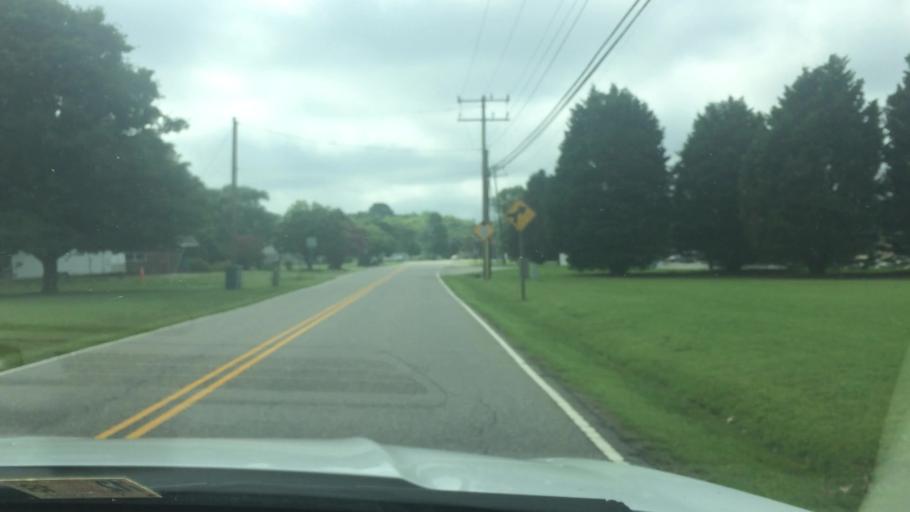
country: US
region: Virginia
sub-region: City of Poquoson
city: Poquoson
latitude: 37.1263
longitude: -76.4348
